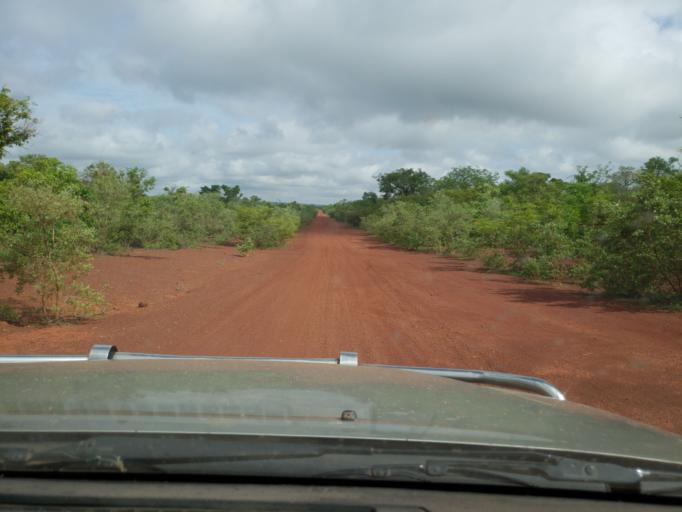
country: ML
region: Segou
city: Bla
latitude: 12.4466
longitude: -6.1429
